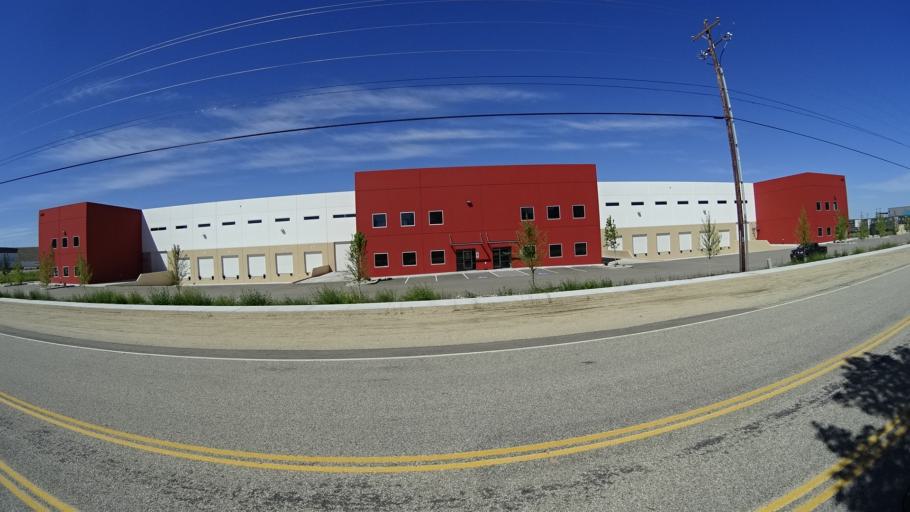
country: US
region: Idaho
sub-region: Ada County
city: Boise
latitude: 43.5250
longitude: -116.1485
